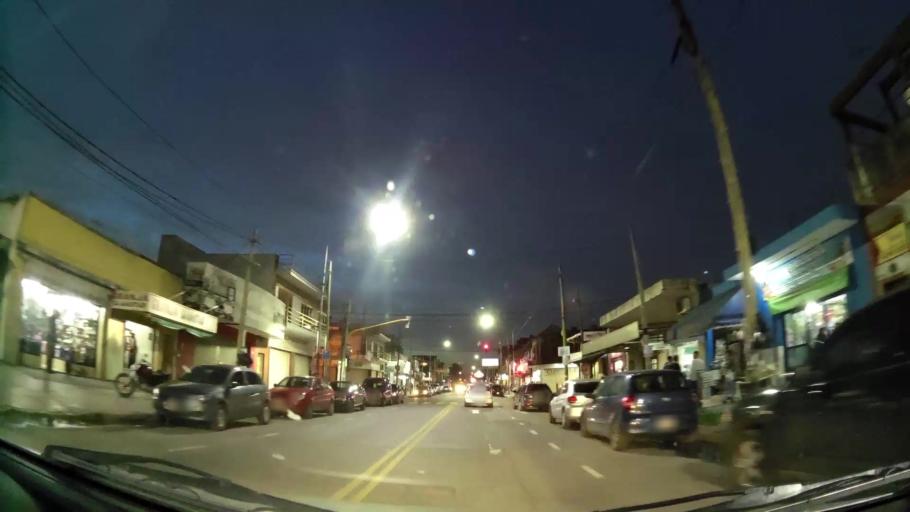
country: AR
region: Buenos Aires
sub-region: Partido de Lanus
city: Lanus
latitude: -34.7289
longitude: -58.3530
